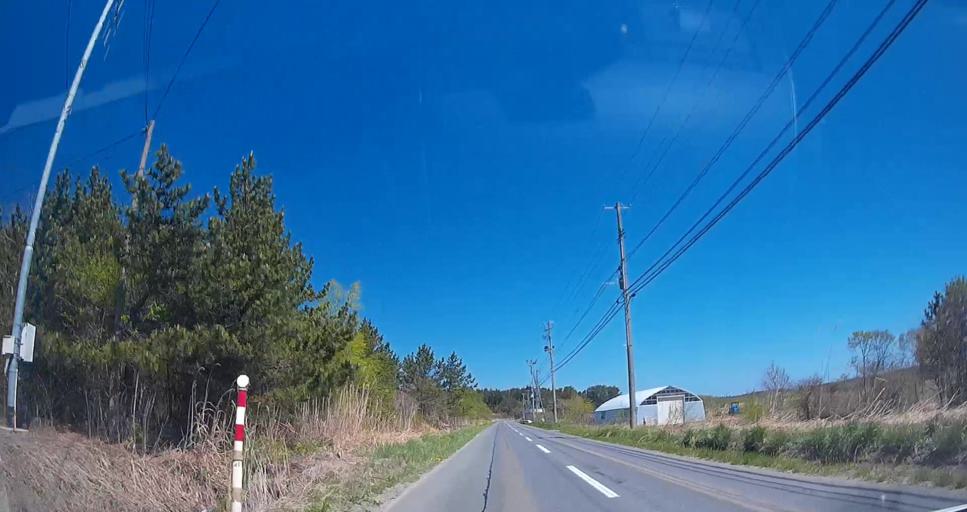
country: JP
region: Aomori
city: Misawa
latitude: 40.8921
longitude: 141.3690
